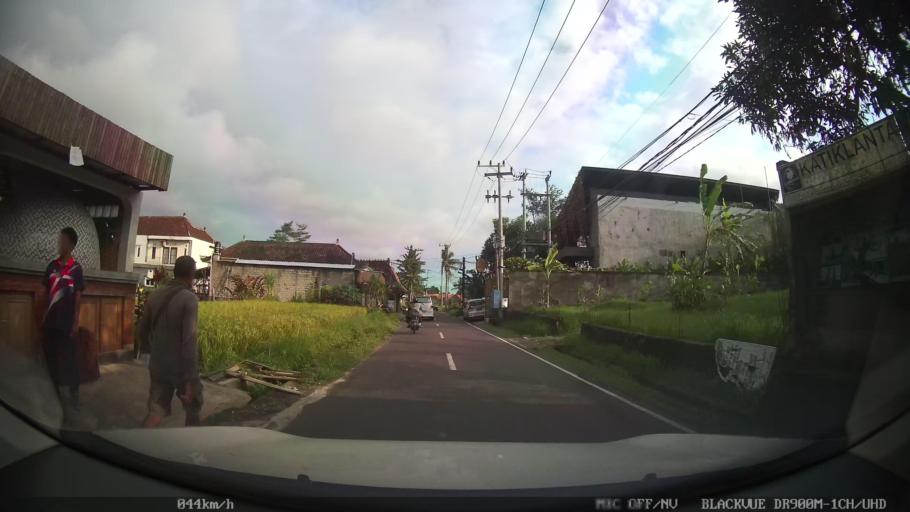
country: ID
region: Bali
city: Banjar Pande
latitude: -8.5145
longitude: 115.2504
